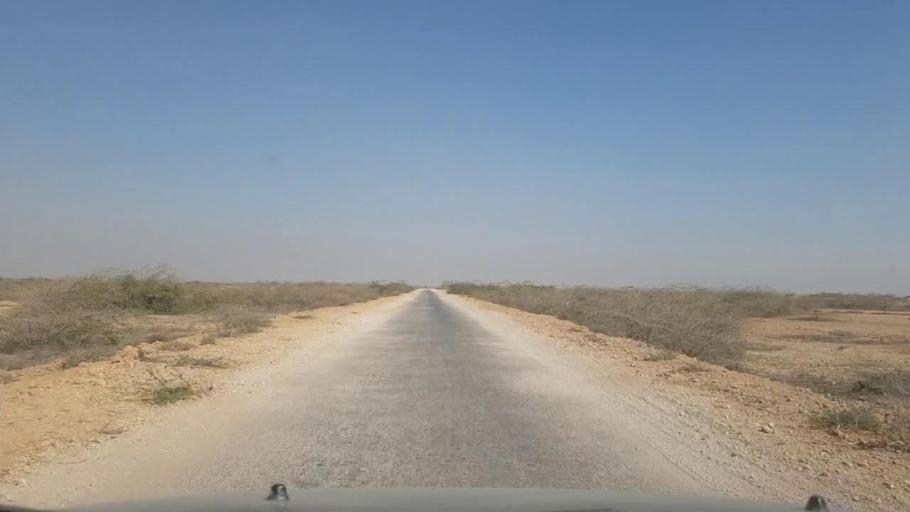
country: PK
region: Sindh
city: Thatta
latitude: 24.9003
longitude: 67.9207
